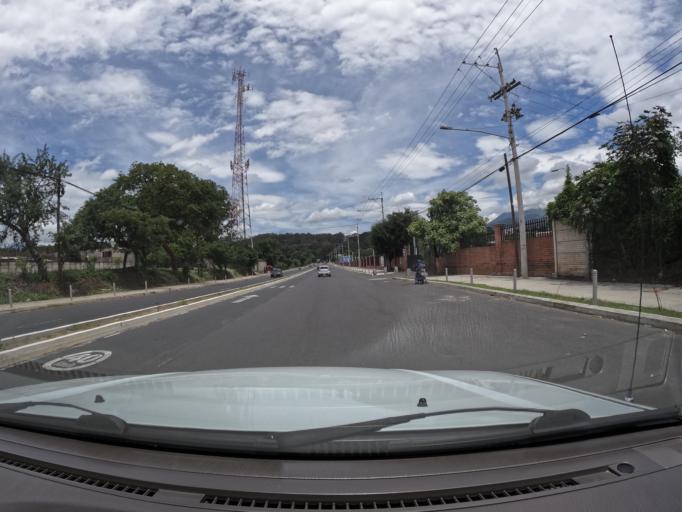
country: GT
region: Guatemala
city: Amatitlan
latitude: 14.5039
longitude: -90.6121
